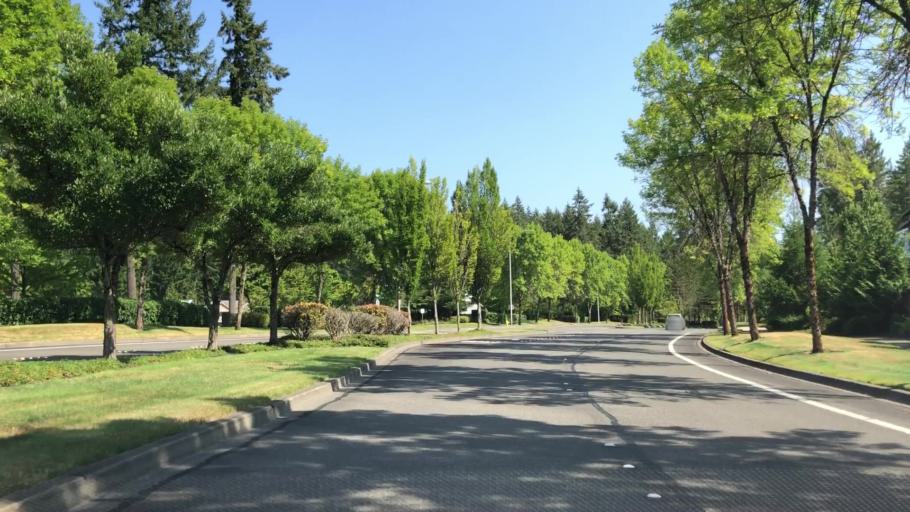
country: US
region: Washington
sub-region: Thurston County
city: Tanglewilde-Thompson Place
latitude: 47.0902
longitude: -122.7582
